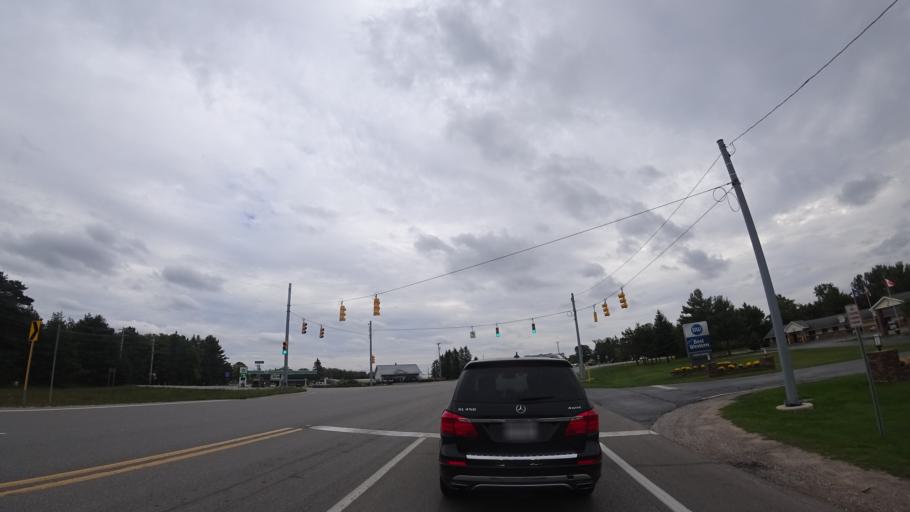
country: US
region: Michigan
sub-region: Emmet County
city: Petoskey
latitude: 45.4277
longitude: -84.9060
